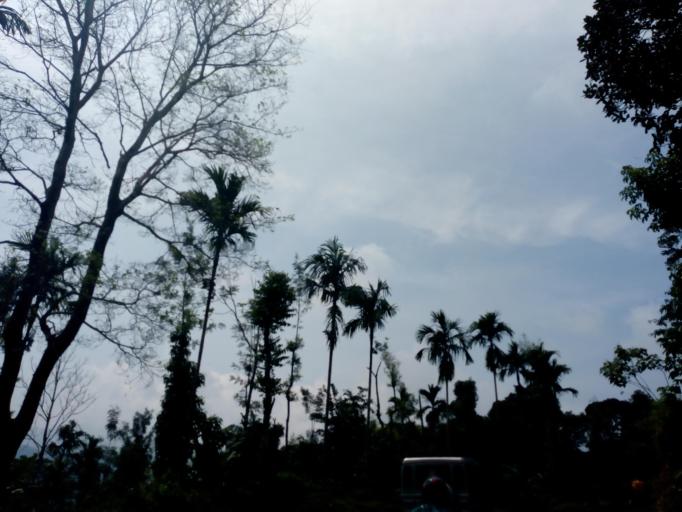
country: IN
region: Karnataka
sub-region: Kodagu
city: Madikeri
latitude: 12.3807
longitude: 75.5192
